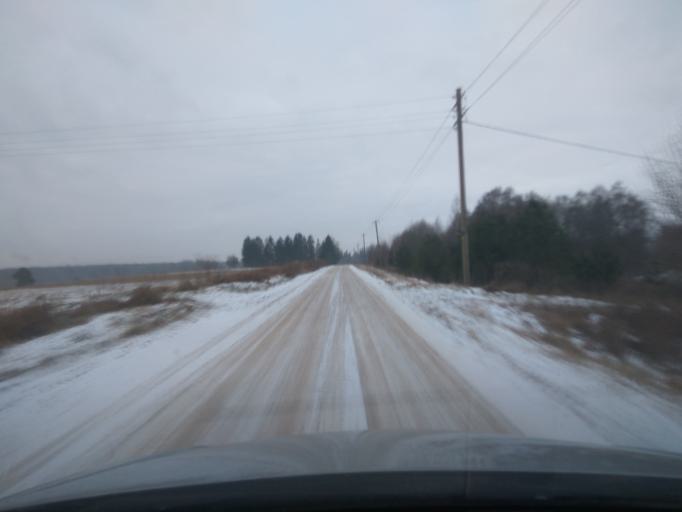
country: LV
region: Aizpute
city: Aizpute
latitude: 56.7602
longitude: 21.7020
